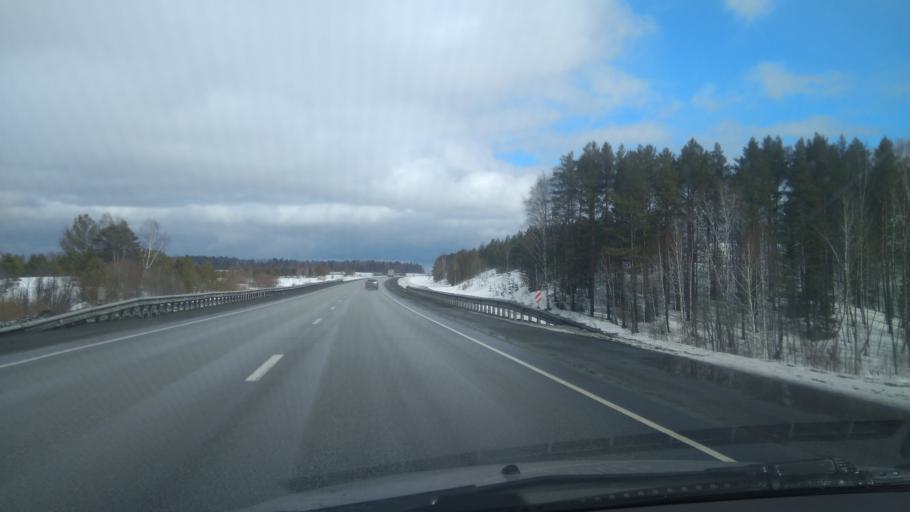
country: RU
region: Sverdlovsk
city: Bisert'
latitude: 56.8058
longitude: 58.7184
